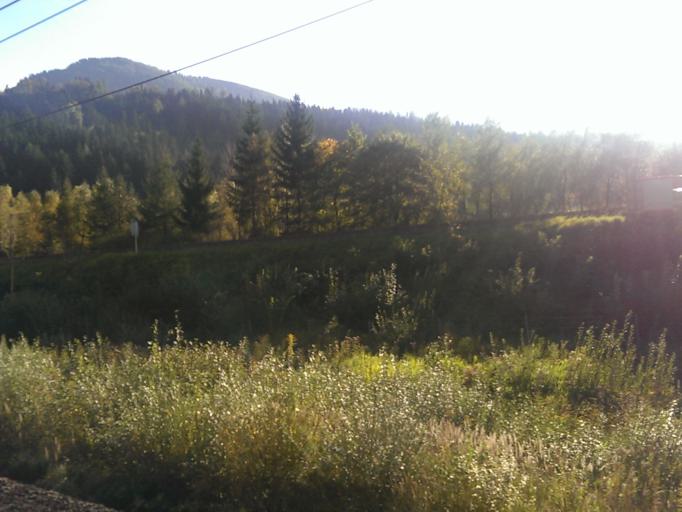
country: AT
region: Styria
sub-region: Politischer Bezirk Liezen
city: Selzthal
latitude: 47.5362
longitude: 14.3093
